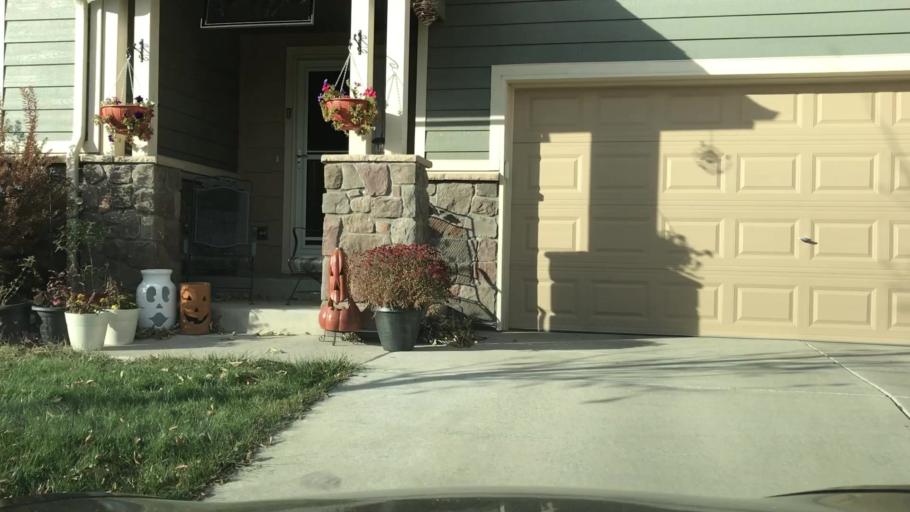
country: US
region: Colorado
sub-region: Larimer County
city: Fort Collins
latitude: 40.5946
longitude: -105.0430
